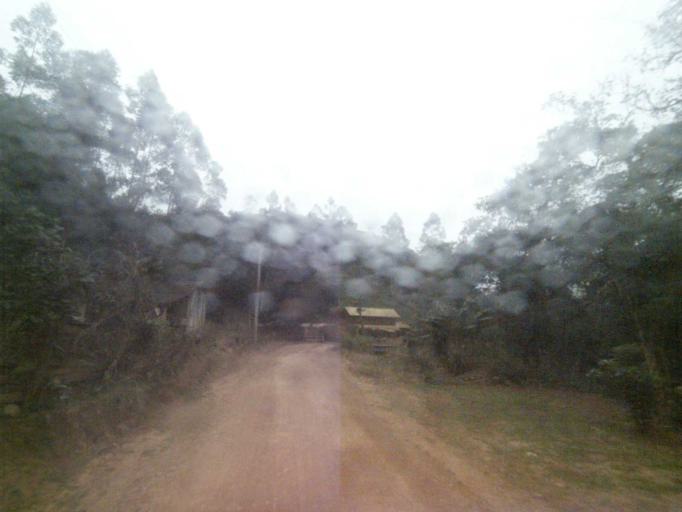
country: BR
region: Santa Catarina
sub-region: Anitapolis
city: Anitapolis
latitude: -27.8674
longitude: -49.1316
